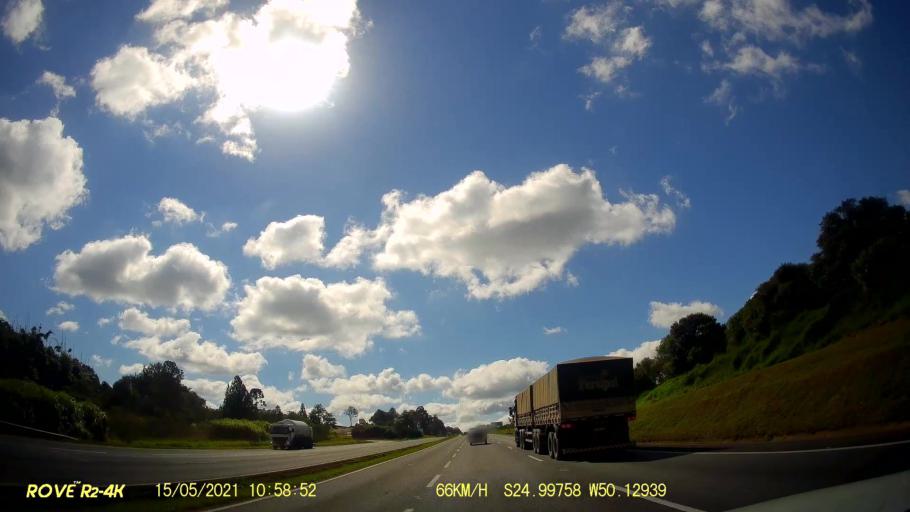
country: BR
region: Parana
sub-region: Carambei
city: Carambei
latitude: -24.9976
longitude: -50.1293
